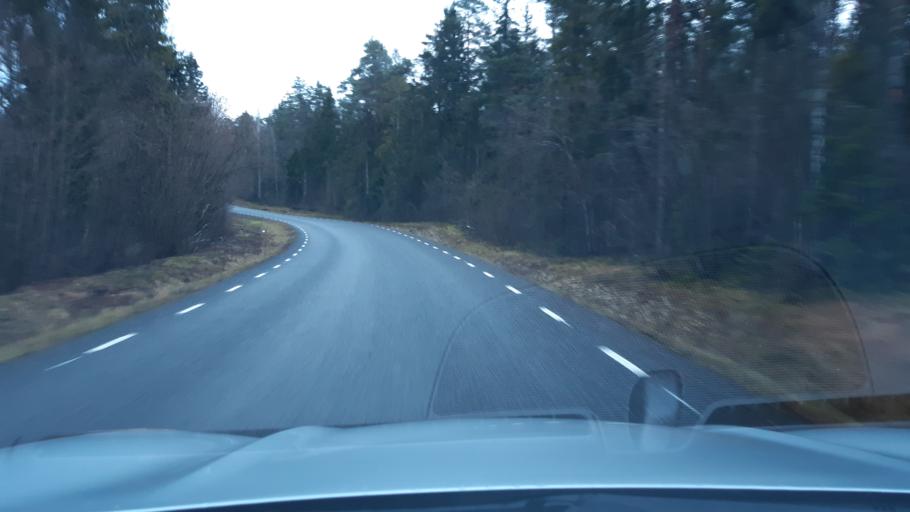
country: EE
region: Harju
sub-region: Saku vald
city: Saku
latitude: 59.1793
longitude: 24.6138
